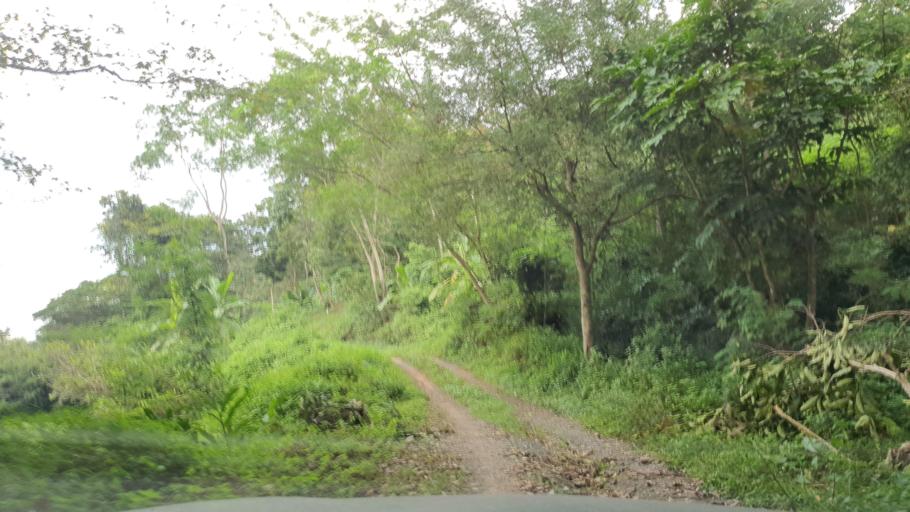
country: TH
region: Chiang Mai
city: Mae On
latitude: 18.8839
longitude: 99.2672
